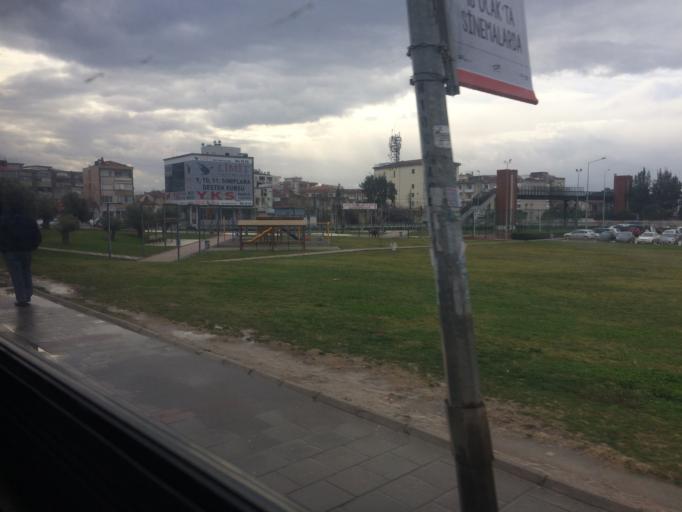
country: TR
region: Izmir
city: Karsiyaka
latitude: 38.4952
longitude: 27.0606
